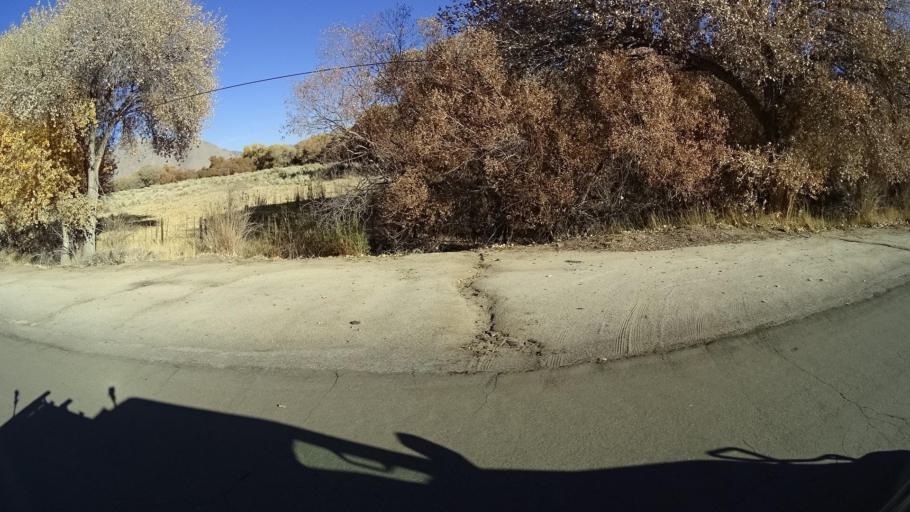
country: US
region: California
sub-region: Kern County
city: Weldon
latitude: 35.6733
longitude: -118.2901
